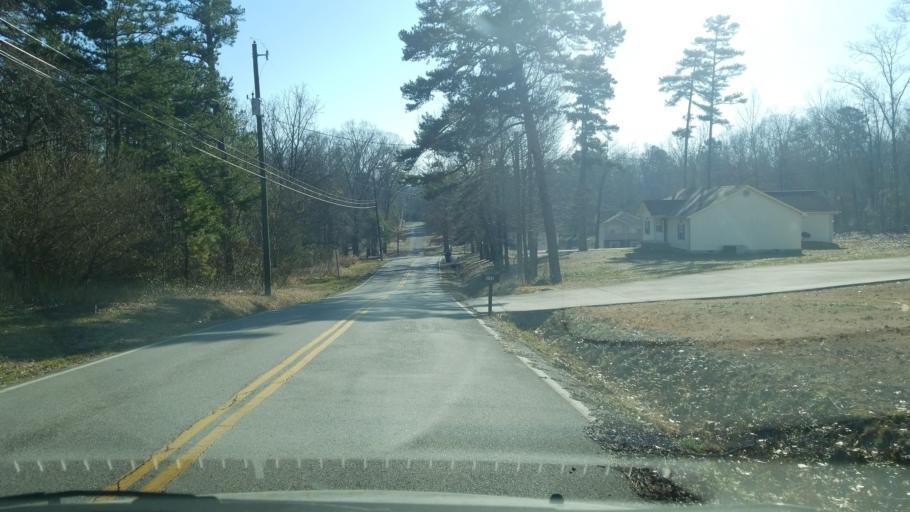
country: US
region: Tennessee
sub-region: Hamilton County
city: Collegedale
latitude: 35.0632
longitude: -85.1034
